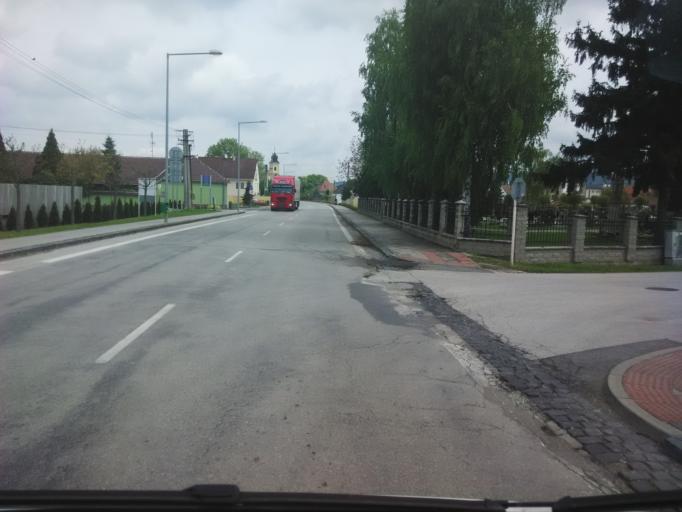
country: SK
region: Trnavsky
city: Leopoldov
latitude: 48.4761
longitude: 17.7780
